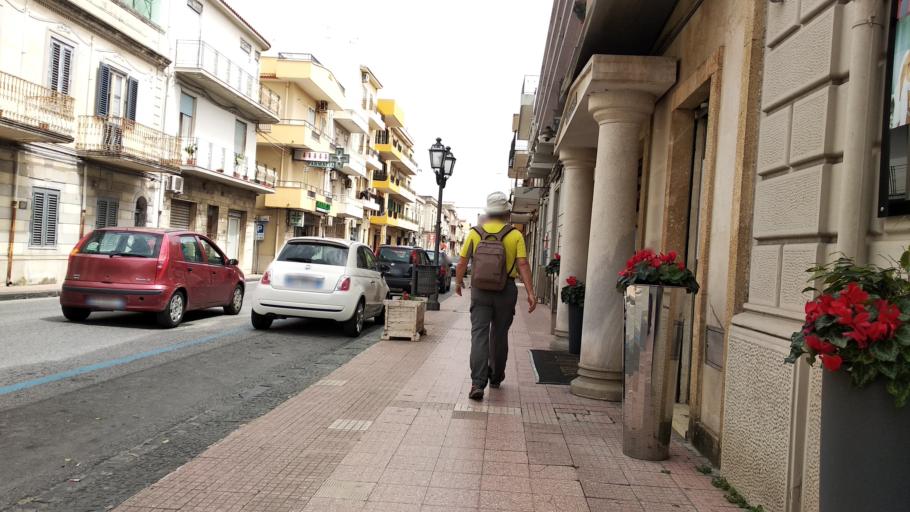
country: IT
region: Sicily
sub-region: Messina
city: Spadafora
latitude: 38.2221
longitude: 15.3778
